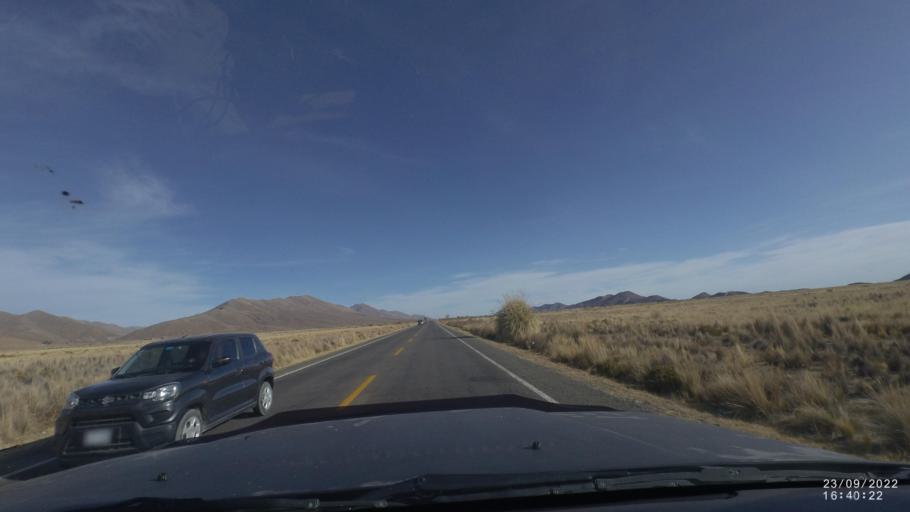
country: BO
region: Oruro
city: Machacamarca
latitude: -18.2751
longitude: -66.9964
